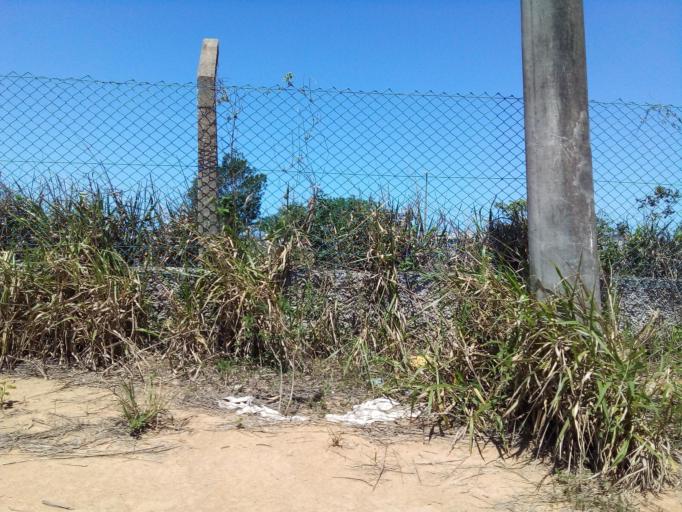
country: BR
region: Espirito Santo
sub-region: Aracruz
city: Aracruz
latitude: -19.8222
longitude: -40.0675
